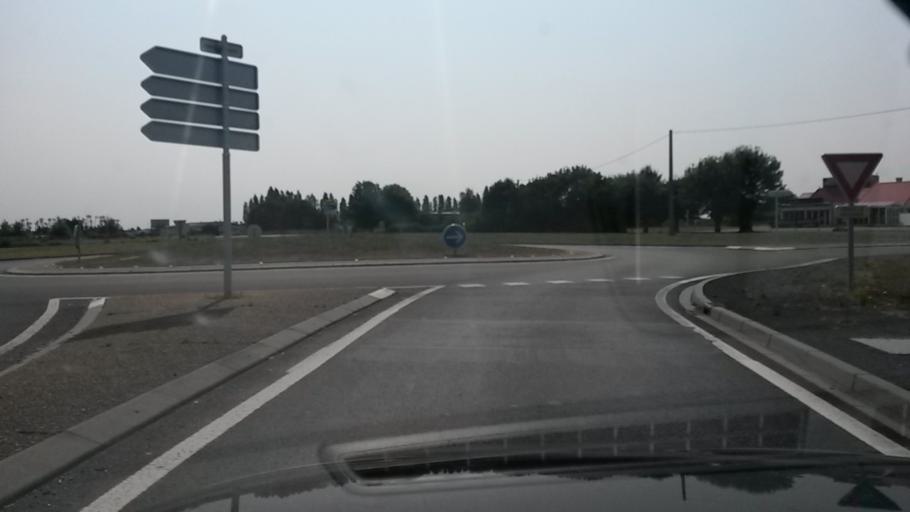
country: FR
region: Pays de la Loire
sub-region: Departement de la Loire-Atlantique
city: Mesanger
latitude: 47.4155
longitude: -1.1885
